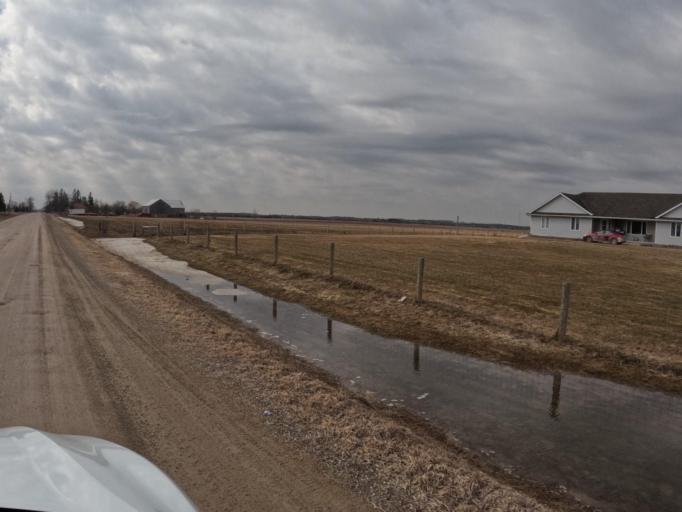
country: CA
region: Ontario
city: Orangeville
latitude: 43.9155
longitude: -80.2168
